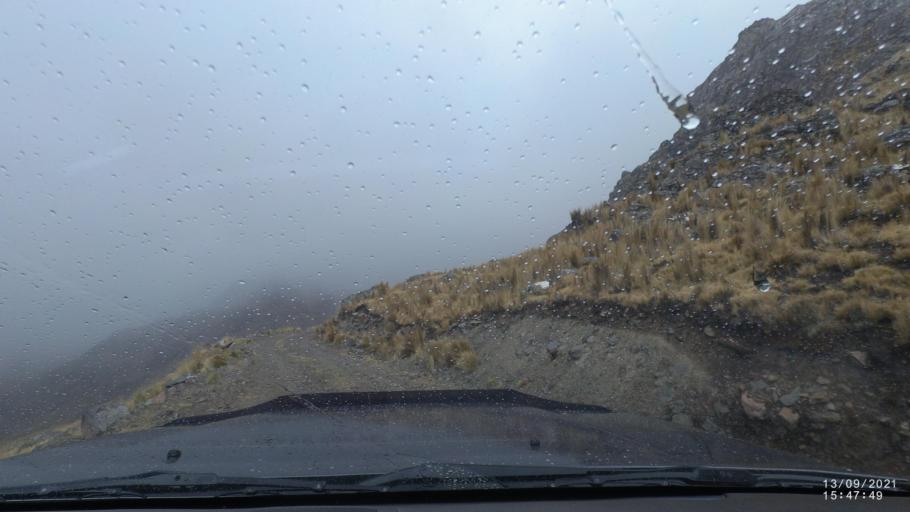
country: BO
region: Cochabamba
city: Colomi
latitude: -17.3127
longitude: -65.7179
